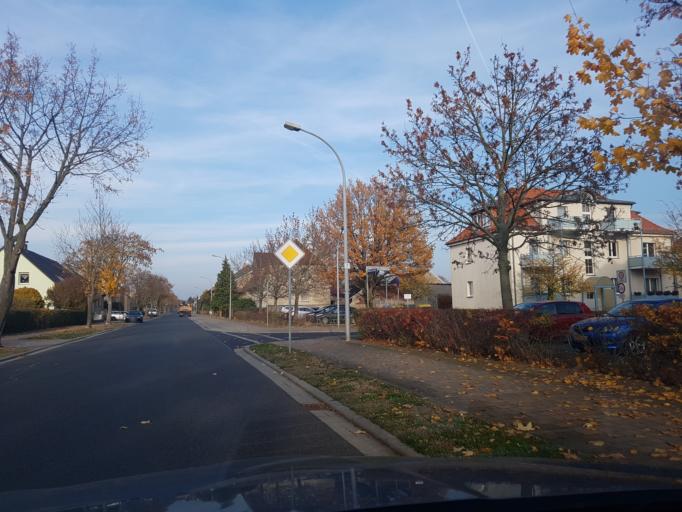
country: DE
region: Brandenburg
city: Falkenberg
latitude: 51.5788
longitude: 13.2318
